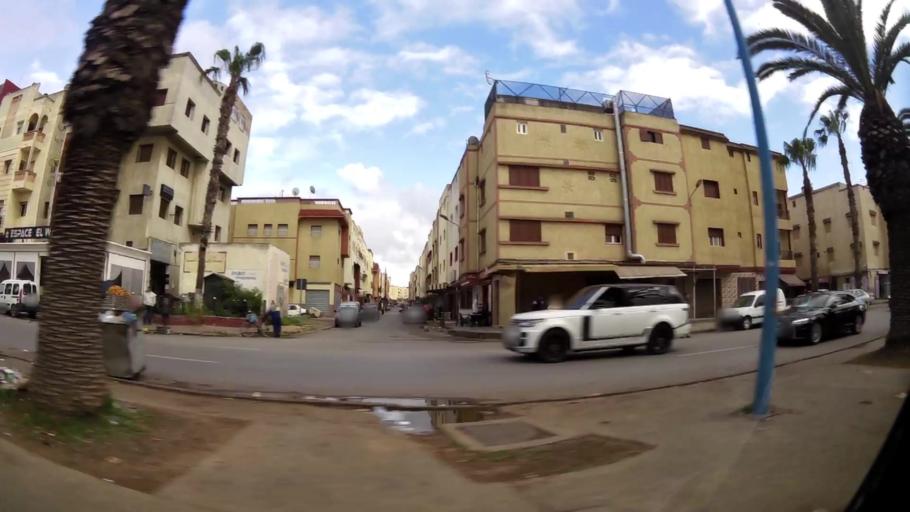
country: MA
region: Grand Casablanca
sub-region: Mohammedia
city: Mohammedia
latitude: 33.6795
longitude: -7.3908
